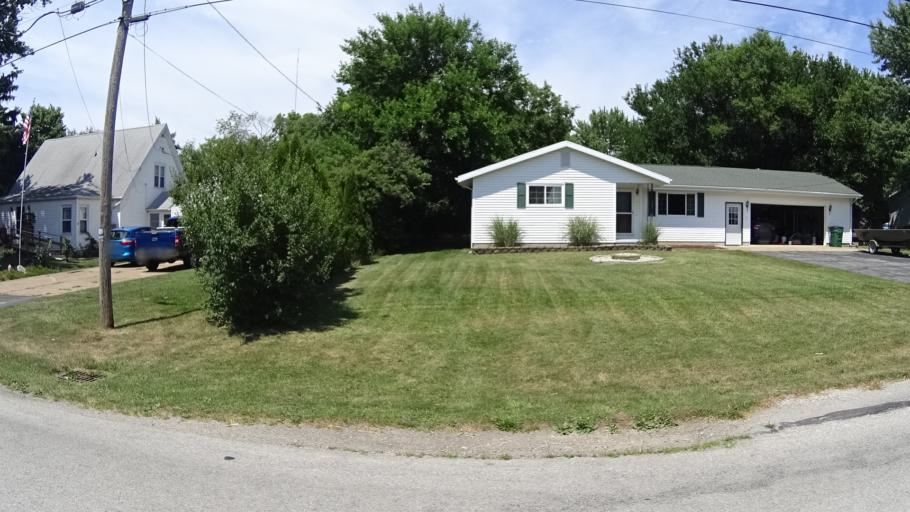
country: US
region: Ohio
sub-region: Erie County
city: Sandusky
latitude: 41.3904
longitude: -82.7898
